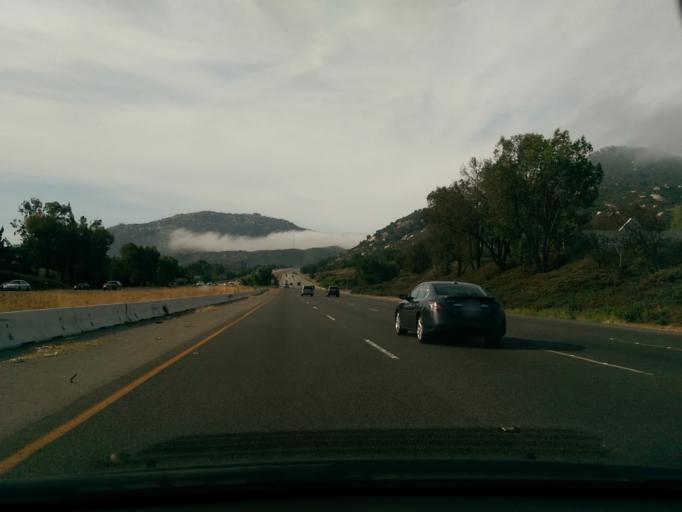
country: US
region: California
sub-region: Riverside County
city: Temecula
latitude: 33.4772
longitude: -117.1397
